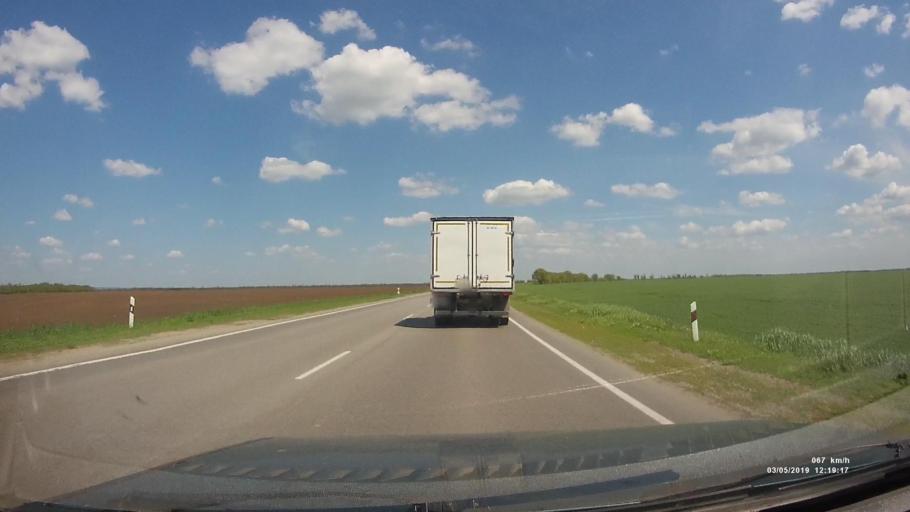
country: RU
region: Rostov
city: Melikhovskaya
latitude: 47.3997
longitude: 40.6067
